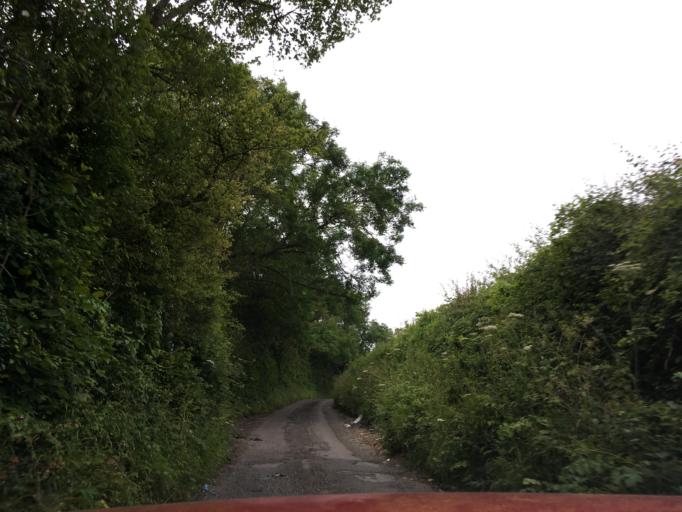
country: GB
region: England
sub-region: Bath and North East Somerset
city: Whitchurch
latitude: 51.3997
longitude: -2.5795
